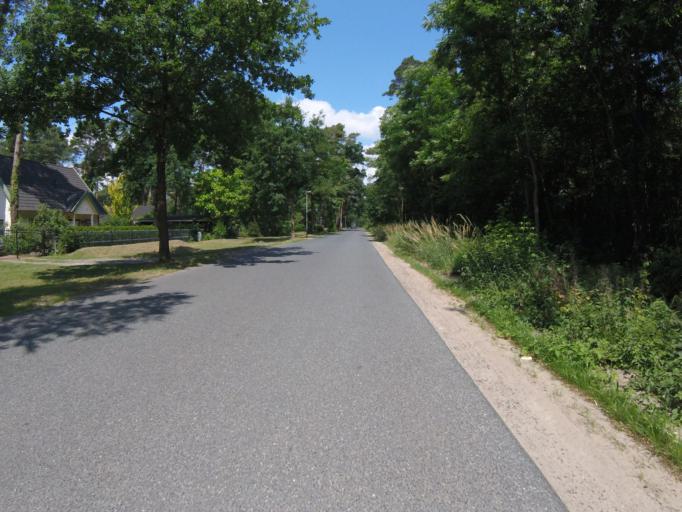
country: DE
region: Brandenburg
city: Bestensee
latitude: 52.2799
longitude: 13.6574
